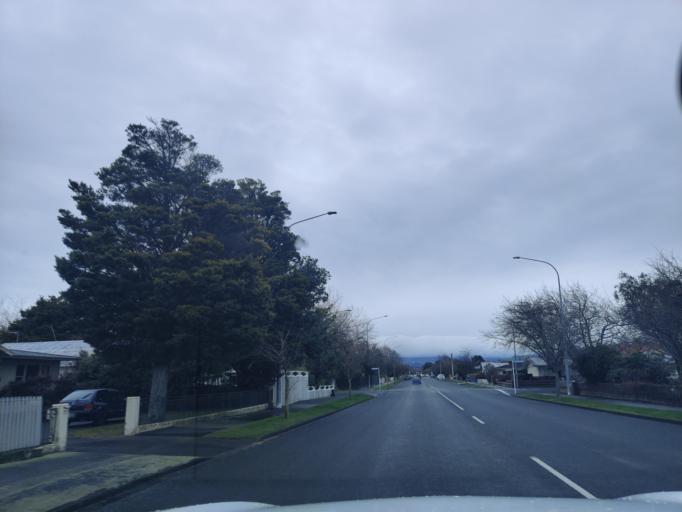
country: NZ
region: Manawatu-Wanganui
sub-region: Palmerston North City
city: Palmerston North
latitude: -40.3427
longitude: 175.6148
